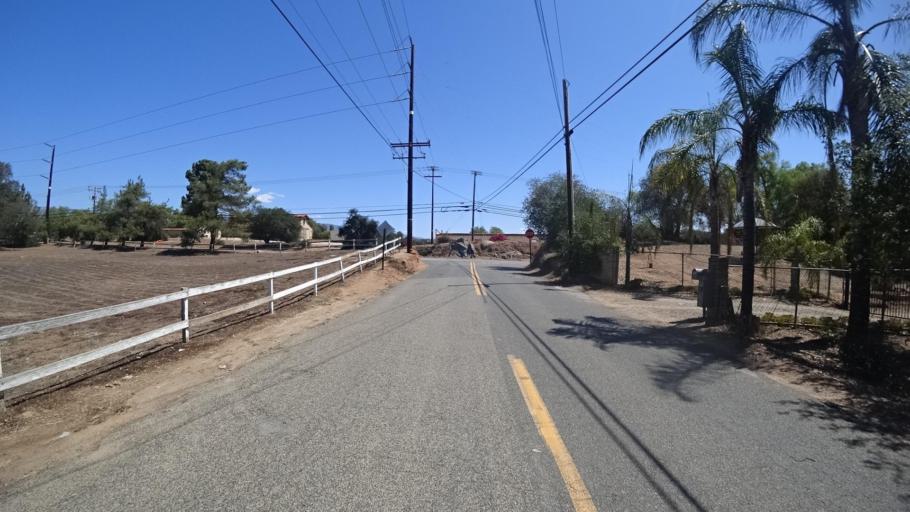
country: US
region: California
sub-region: San Diego County
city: Valley Center
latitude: 33.2710
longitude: -117.0240
